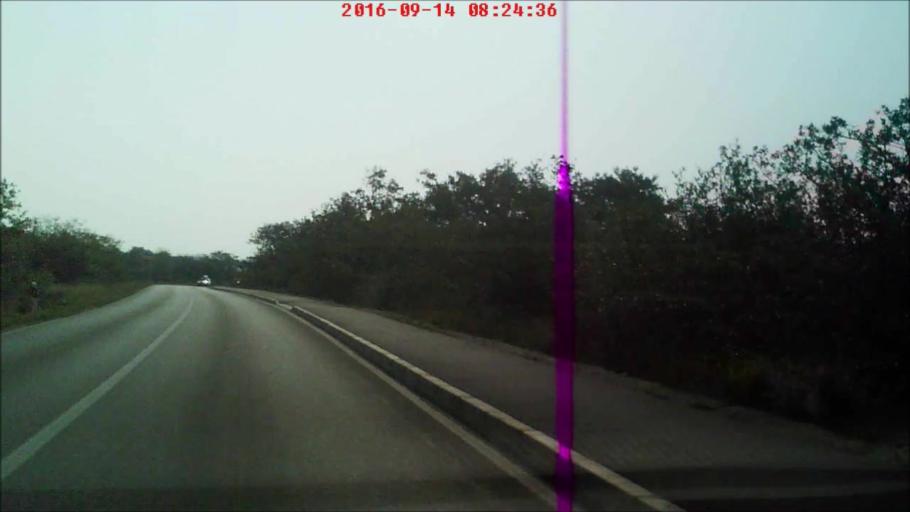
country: HR
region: Zadarska
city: Vrsi
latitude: 44.2062
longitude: 15.2461
